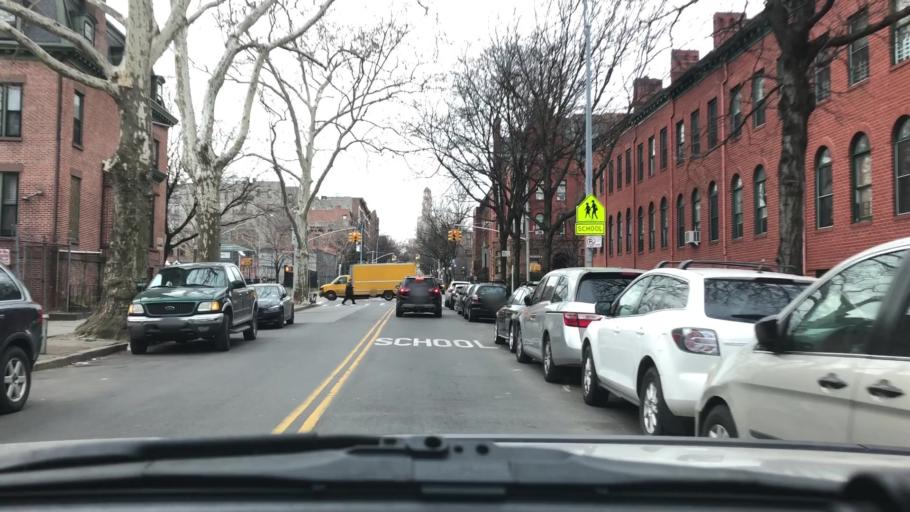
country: US
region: New York
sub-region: Kings County
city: Brooklyn
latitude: 40.6869
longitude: -73.9648
